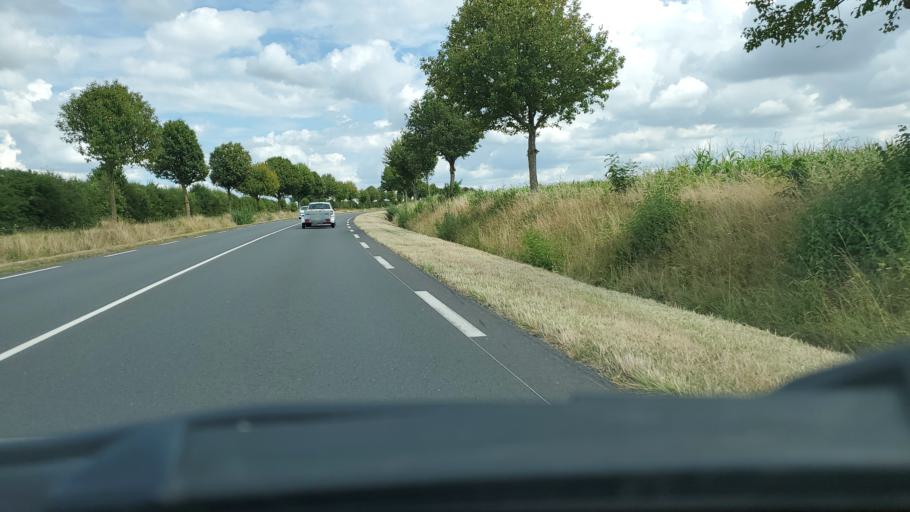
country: FR
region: Ile-de-France
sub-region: Departement de Seine-et-Marne
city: Nanteuil-les-Meaux
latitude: 48.9141
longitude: 2.9081
